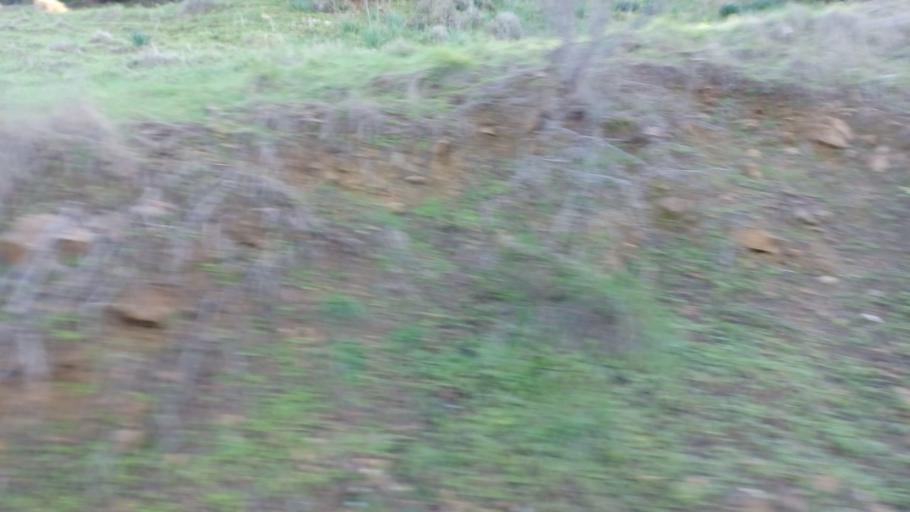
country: CY
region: Limassol
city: Pachna
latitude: 34.8138
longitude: 32.6547
